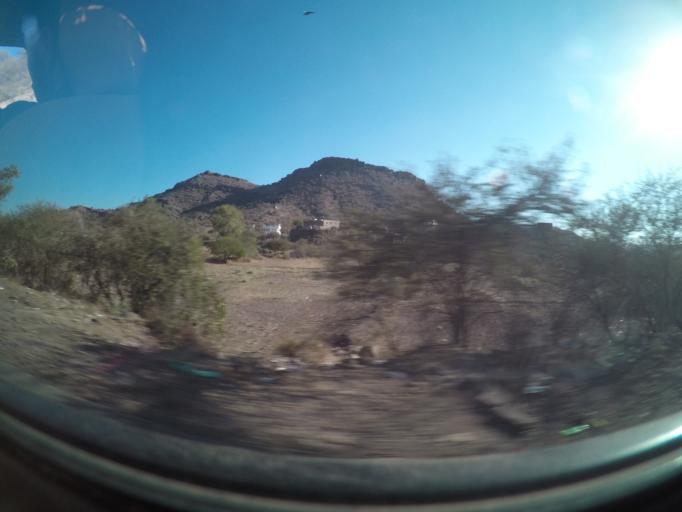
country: YE
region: Ad Dali'
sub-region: Ad Dhale'e
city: Dhalie
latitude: 13.6738
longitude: 44.7610
